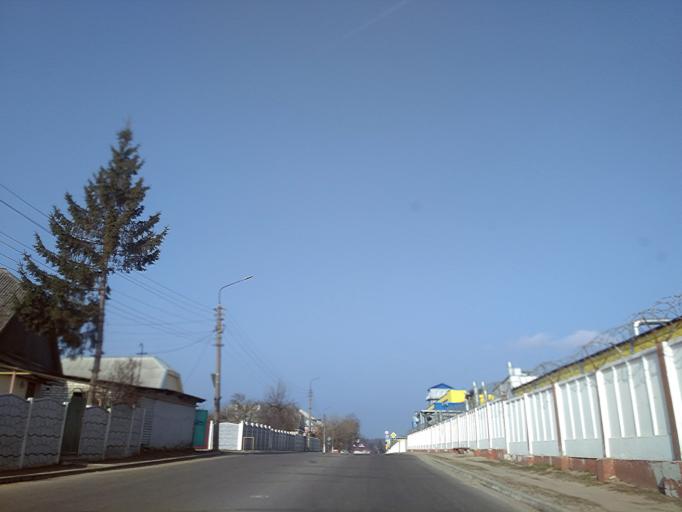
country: BY
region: Minsk
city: Horad Barysaw
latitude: 54.2255
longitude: 28.5288
